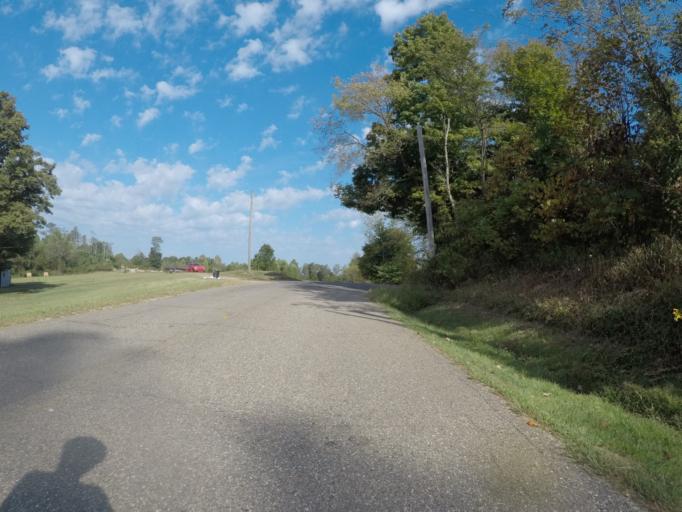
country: US
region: West Virginia
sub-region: Cabell County
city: Lesage
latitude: 38.5948
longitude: -82.4196
